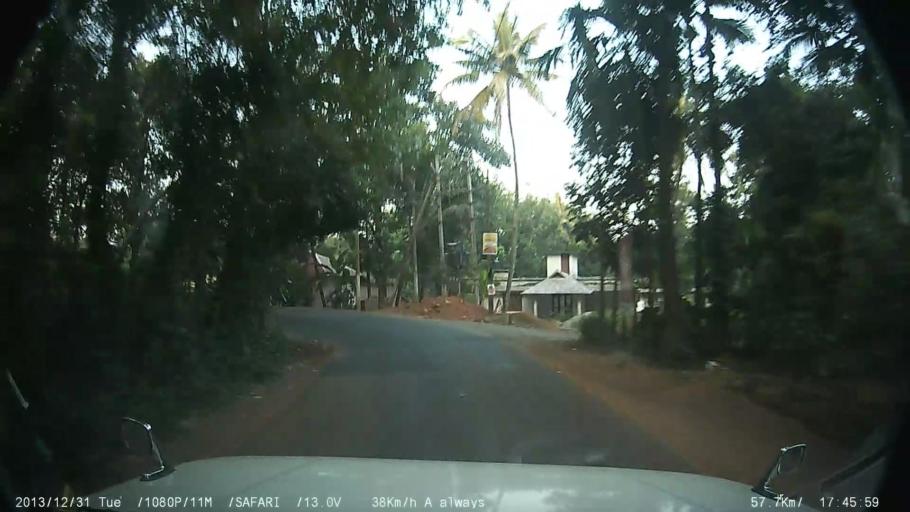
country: IN
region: Kerala
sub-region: Kottayam
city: Vaikam
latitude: 9.7334
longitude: 76.4790
